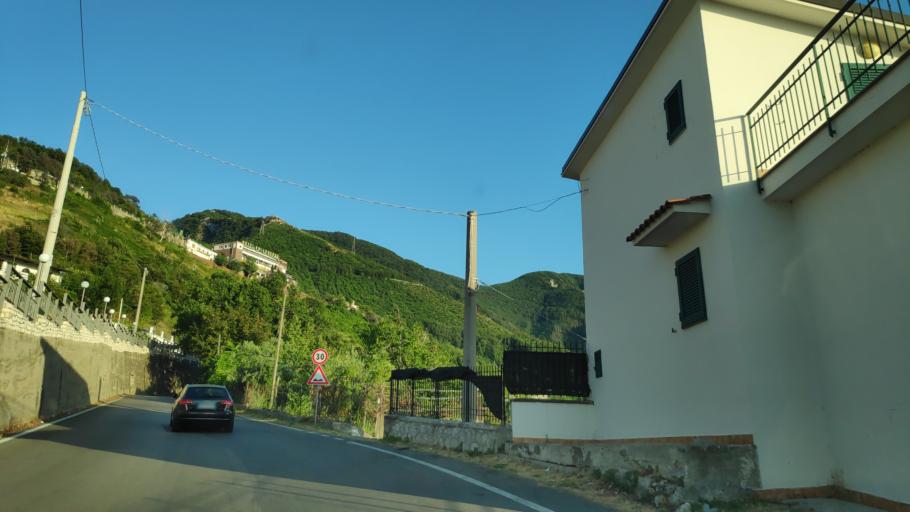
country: IT
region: Campania
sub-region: Provincia di Salerno
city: Corbara
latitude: 40.7266
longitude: 14.5981
